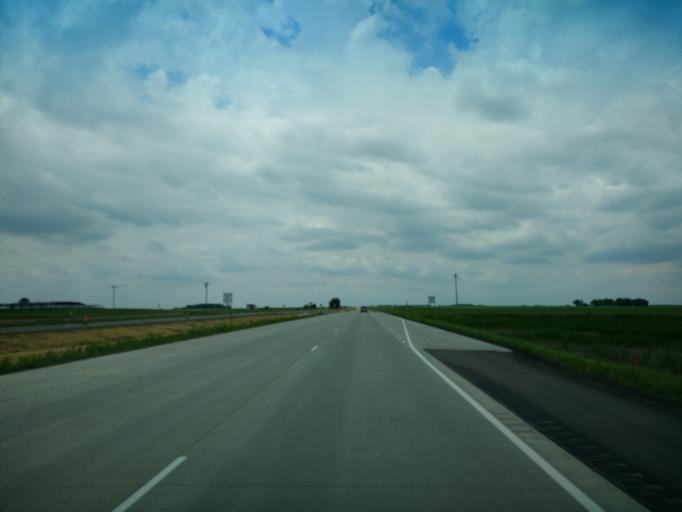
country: US
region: Minnesota
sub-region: Cottonwood County
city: Mountain Lake
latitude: 43.9248
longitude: -94.9773
